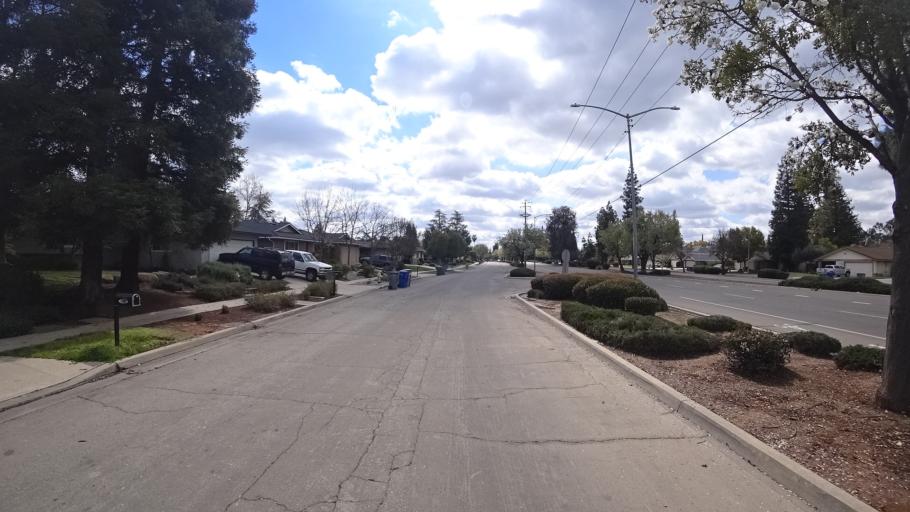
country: US
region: California
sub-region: Fresno County
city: Fresno
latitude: 36.8353
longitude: -119.8262
